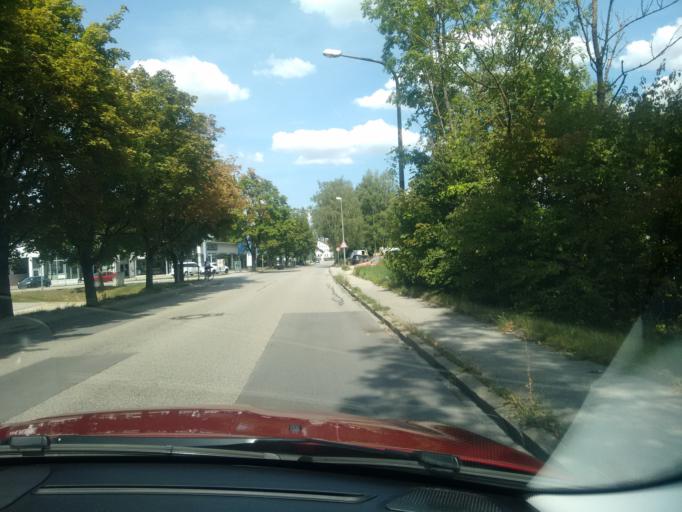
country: DE
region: Bavaria
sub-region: Upper Bavaria
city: Trostberg an der Alz
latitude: 48.0229
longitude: 12.5531
